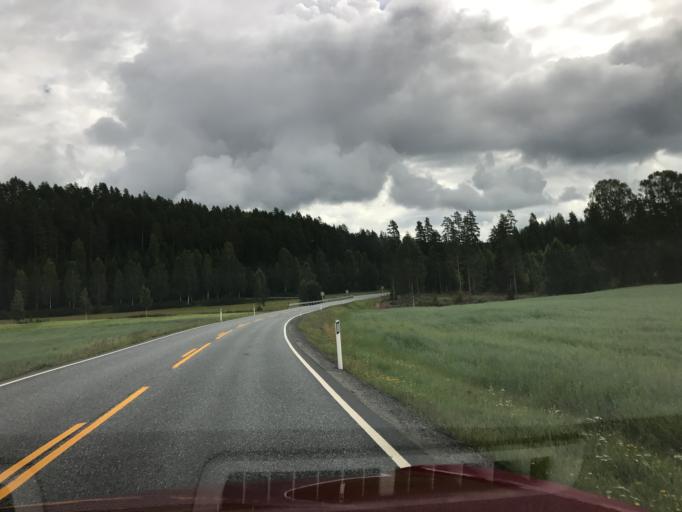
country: NO
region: Buskerud
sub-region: Flesberg
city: Lampeland
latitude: 59.8409
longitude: 9.5469
